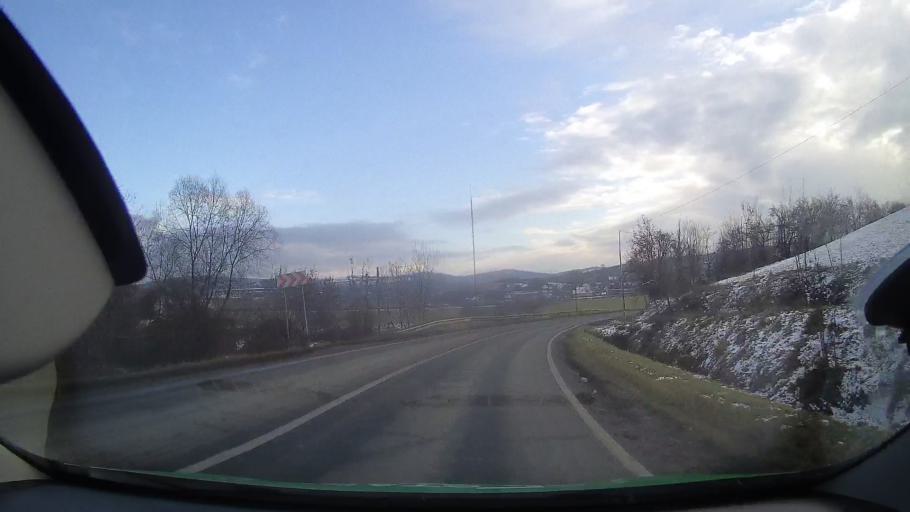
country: RO
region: Mures
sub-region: Comuna Cucerdea
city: Cucerdea
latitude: 46.4097
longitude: 24.2677
